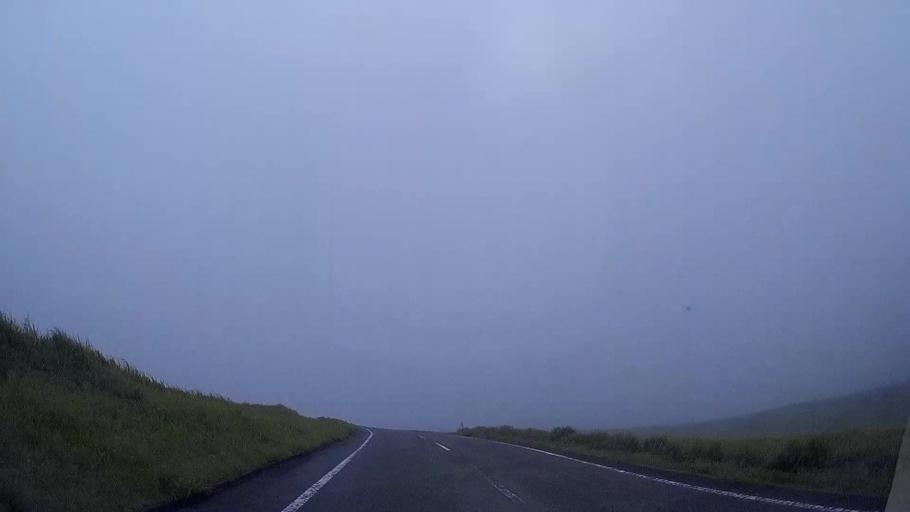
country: JP
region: Kumamoto
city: Aso
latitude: 33.0001
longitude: 131.0730
